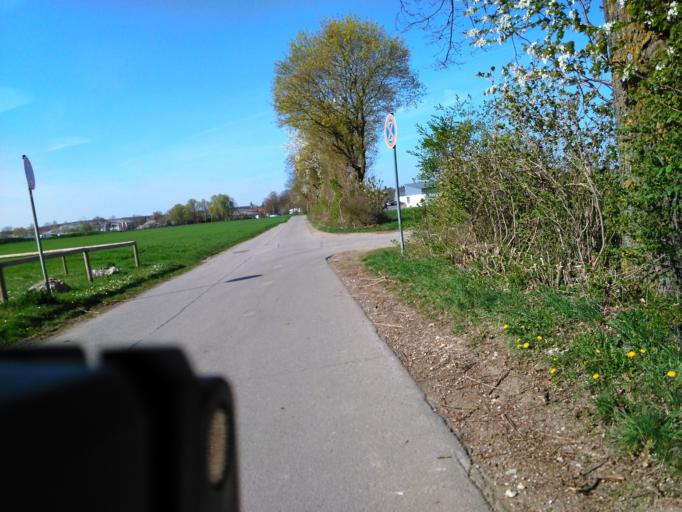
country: DE
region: Bavaria
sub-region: Upper Bavaria
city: Mammendorf
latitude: 48.2031
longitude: 11.1751
